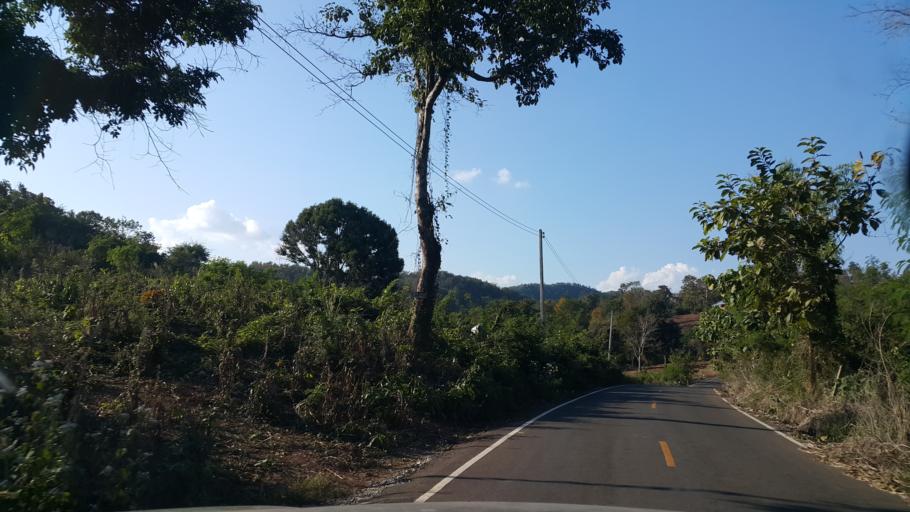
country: TH
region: Sukhothai
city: Thung Saliam
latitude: 17.3899
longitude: 99.5090
